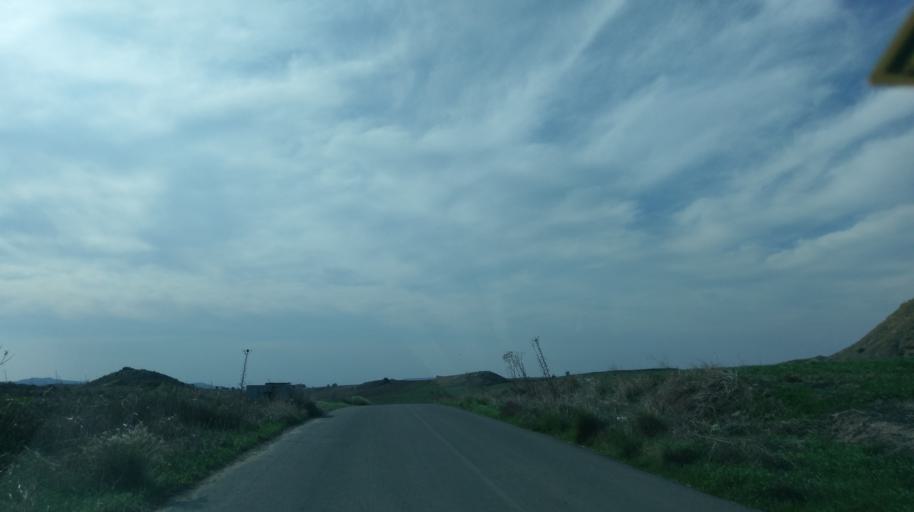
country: CY
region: Keryneia
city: Lapithos
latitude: 35.2807
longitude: 33.1930
